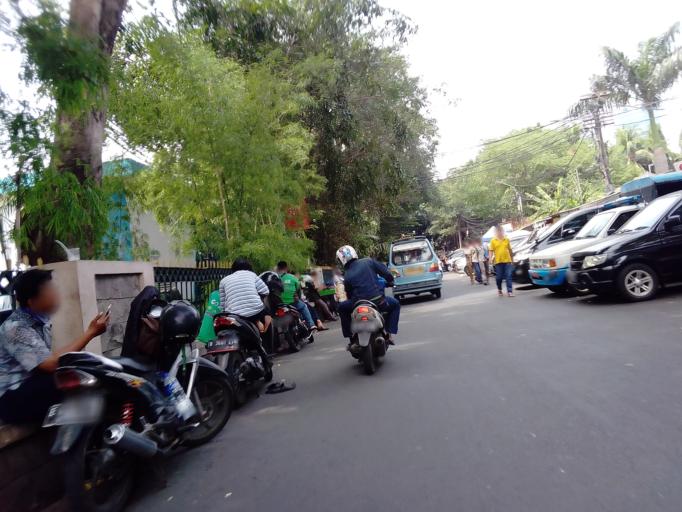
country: ID
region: Jakarta Raya
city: Jakarta
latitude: -6.1823
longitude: 106.8109
